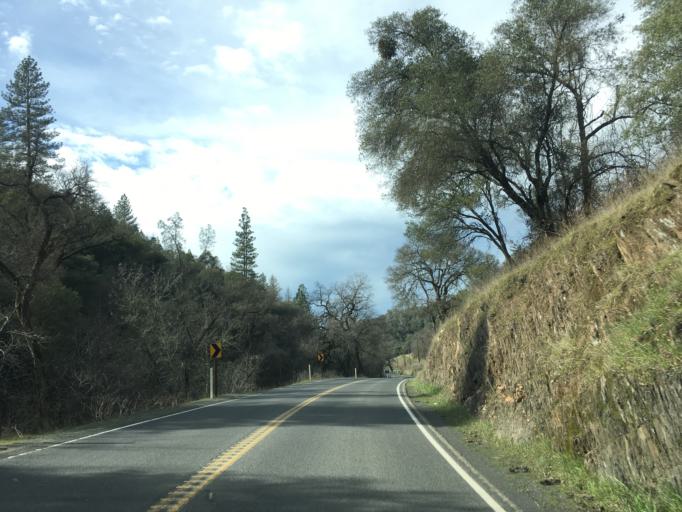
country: US
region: California
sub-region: Calaveras County
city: Mountain Ranch
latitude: 38.1917
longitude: -120.5966
